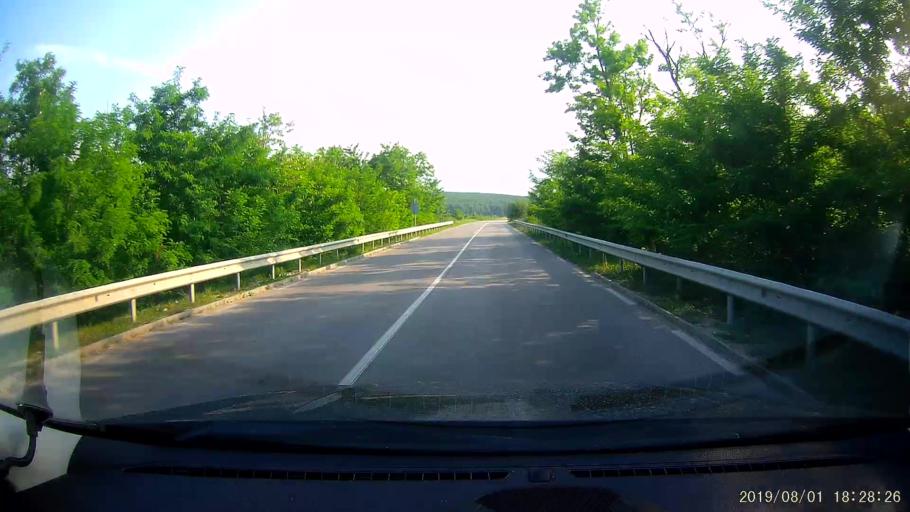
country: BG
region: Shumen
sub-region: Obshtina Venets
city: Venets
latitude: 43.5750
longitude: 26.9646
